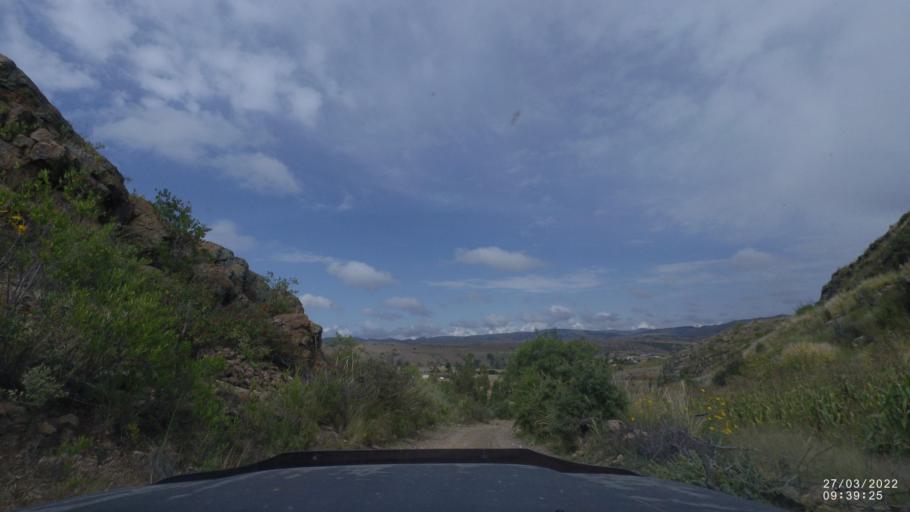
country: BO
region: Cochabamba
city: Cliza
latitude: -17.7499
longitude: -65.8977
